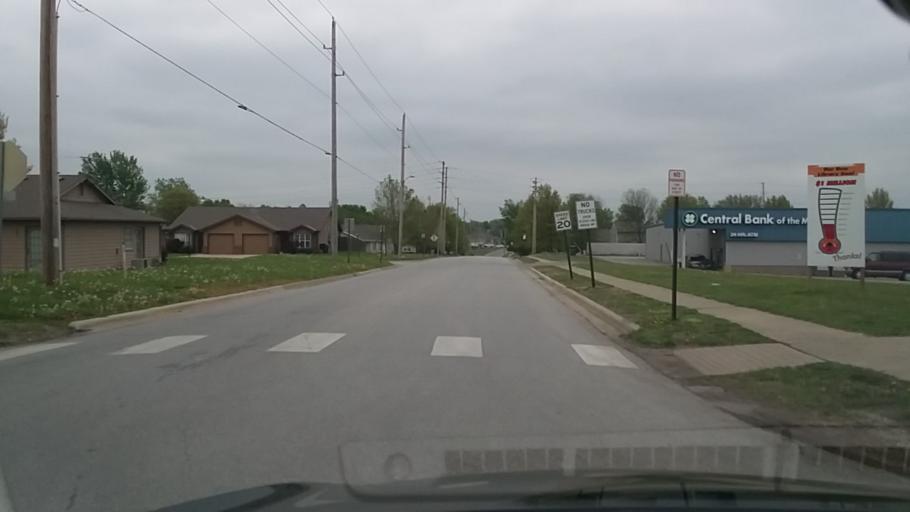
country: US
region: Kansas
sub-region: Douglas County
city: Eudora
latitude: 38.9357
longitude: -95.0959
